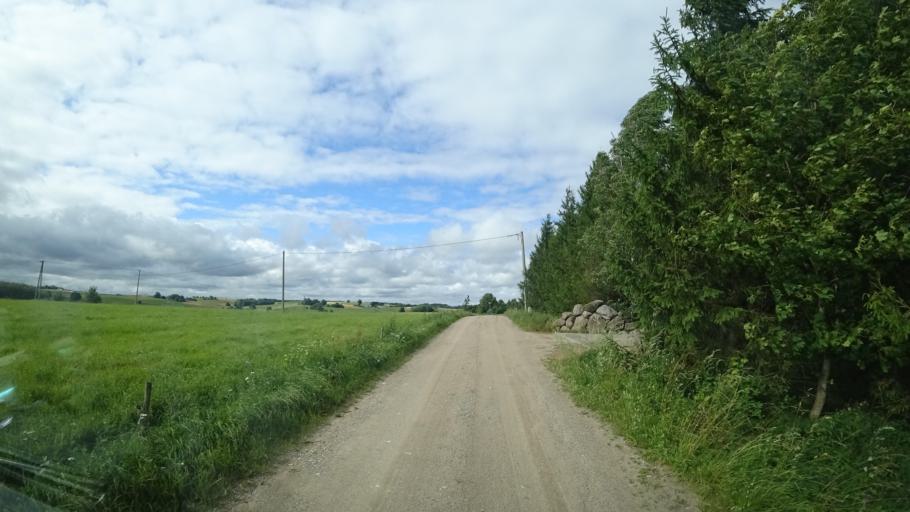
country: LT
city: Virbalis
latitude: 54.3756
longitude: 22.9023
